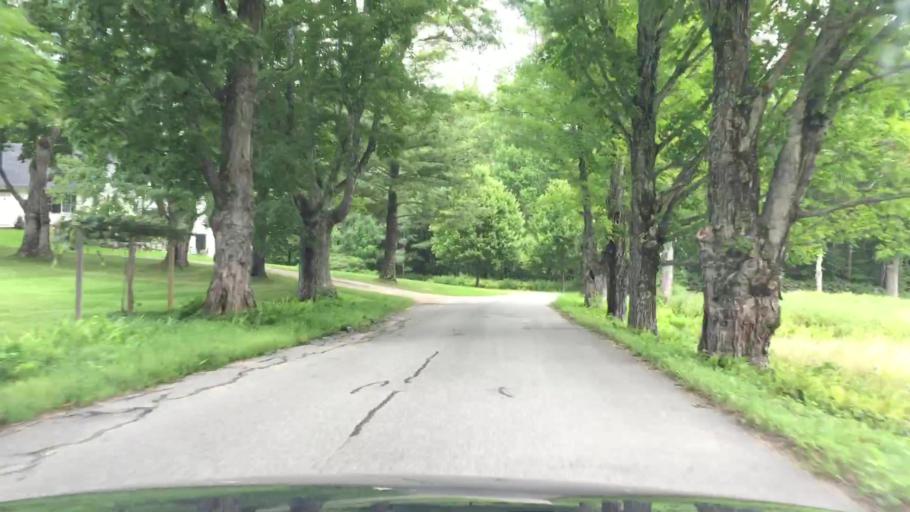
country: US
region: New Hampshire
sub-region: Carroll County
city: Sandwich
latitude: 43.7923
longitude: -71.4787
